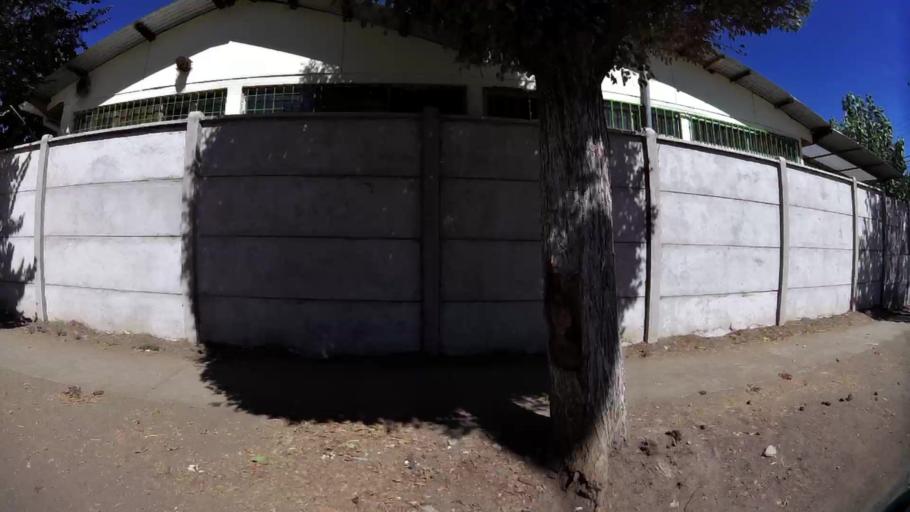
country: CL
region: O'Higgins
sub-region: Provincia de Cachapoal
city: Graneros
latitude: -33.9714
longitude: -70.7106
